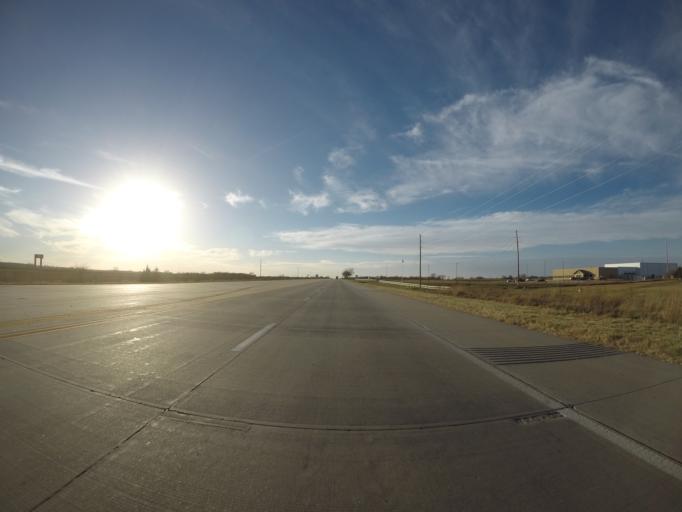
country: US
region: Kansas
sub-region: Lyon County
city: Emporia
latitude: 38.4123
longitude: -96.2460
